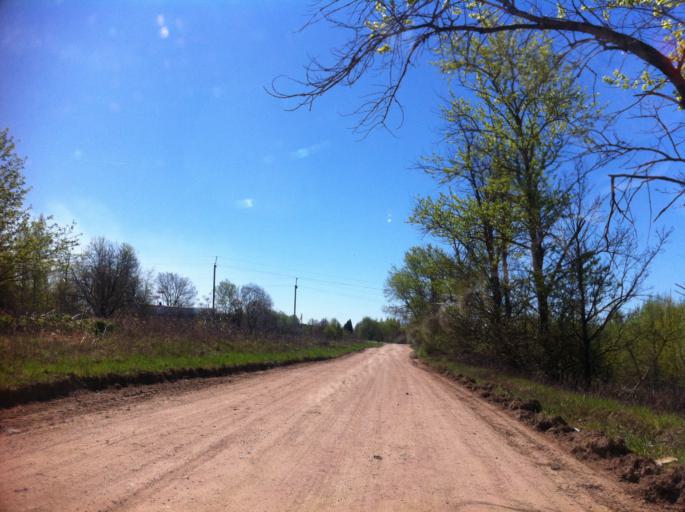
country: RU
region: Pskov
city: Izborsk
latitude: 57.7897
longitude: 27.9631
